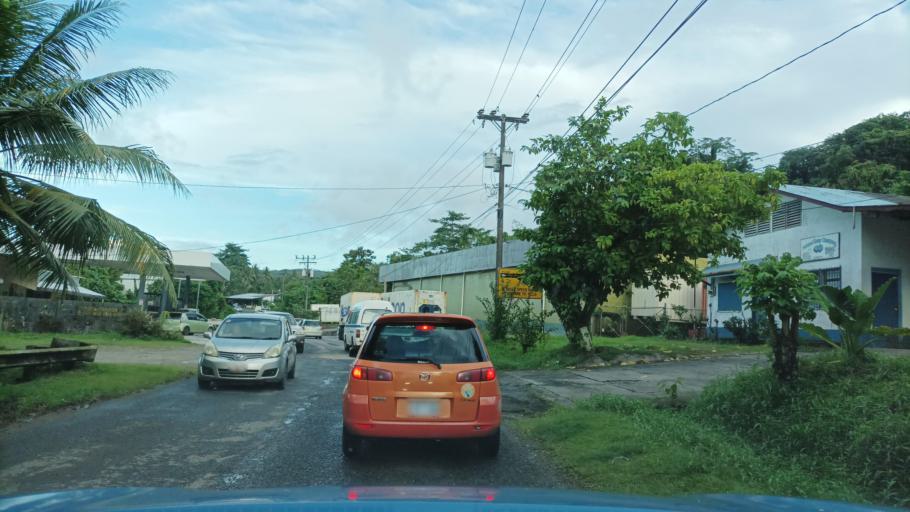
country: FM
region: Pohnpei
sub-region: Kolonia Municipality
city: Kolonia Town
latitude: 6.9569
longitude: 158.2041
